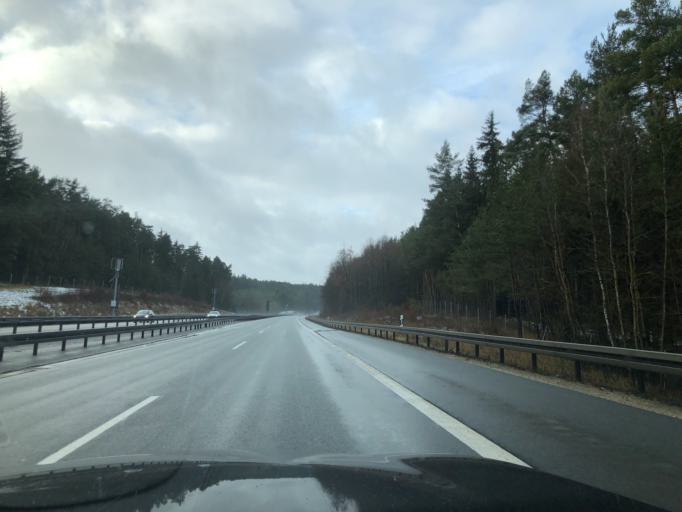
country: DE
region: Bavaria
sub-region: Upper Palatinate
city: Amberg
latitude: 49.3987
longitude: 11.8453
